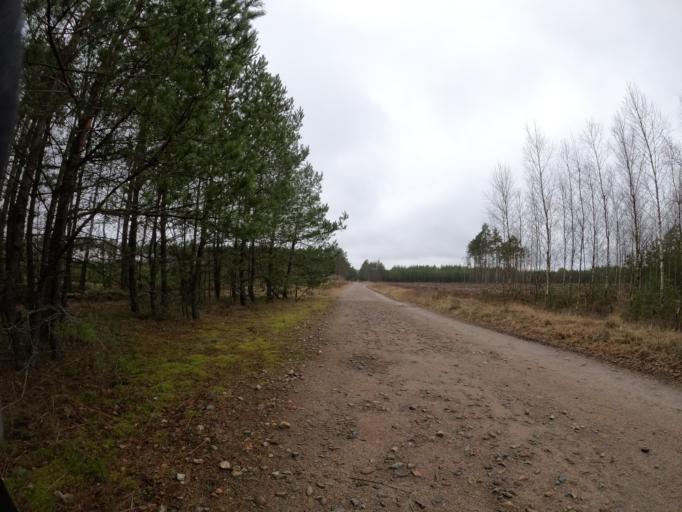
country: PL
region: Greater Poland Voivodeship
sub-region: Powiat zlotowski
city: Sypniewo
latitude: 53.5074
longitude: 16.5617
